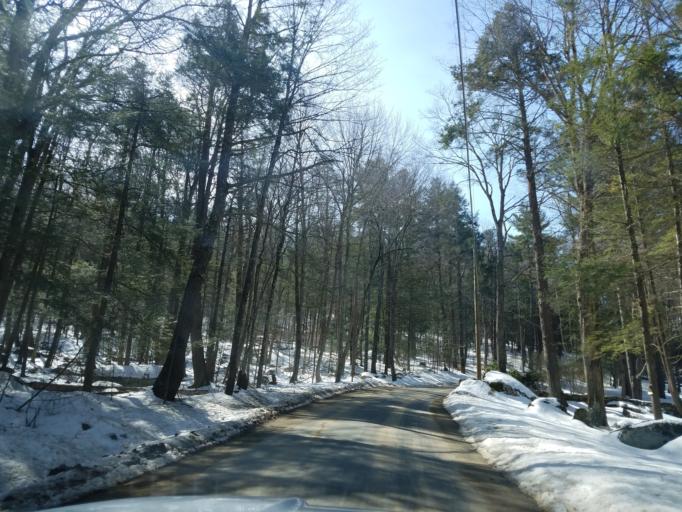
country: US
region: Connecticut
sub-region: Litchfield County
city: Canaan
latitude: 41.8722
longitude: -73.3525
